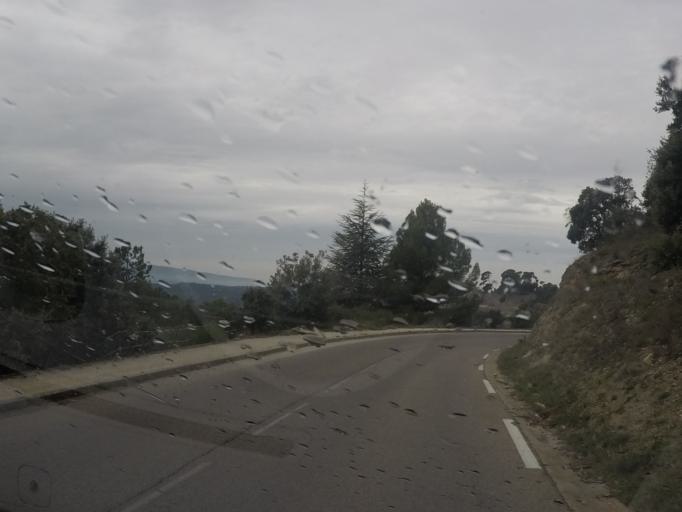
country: FR
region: Provence-Alpes-Cote d'Azur
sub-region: Departement du Vaucluse
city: Bonnieux
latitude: 43.8212
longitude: 5.3160
